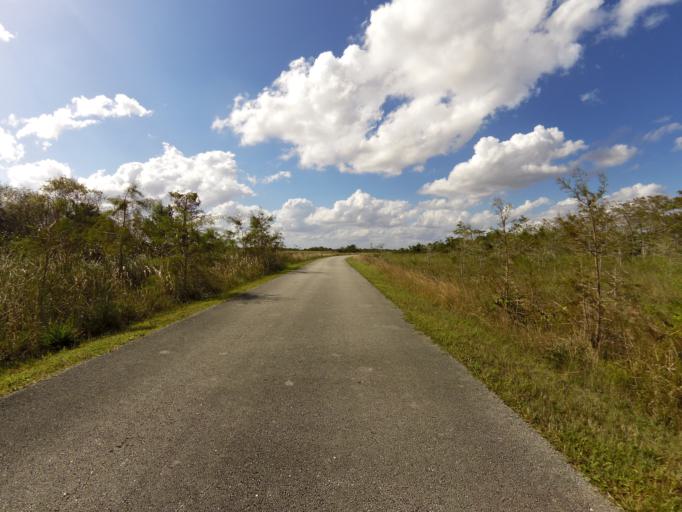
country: US
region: Florida
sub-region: Miami-Dade County
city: The Hammocks
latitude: 25.7175
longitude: -80.7607
